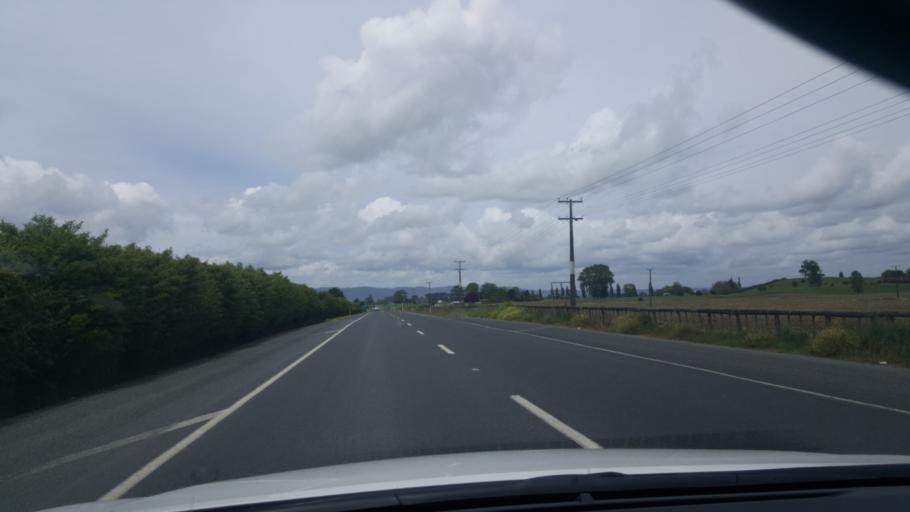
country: NZ
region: Waikato
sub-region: Matamata-Piako District
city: Matamata
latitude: -37.8864
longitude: 175.7692
